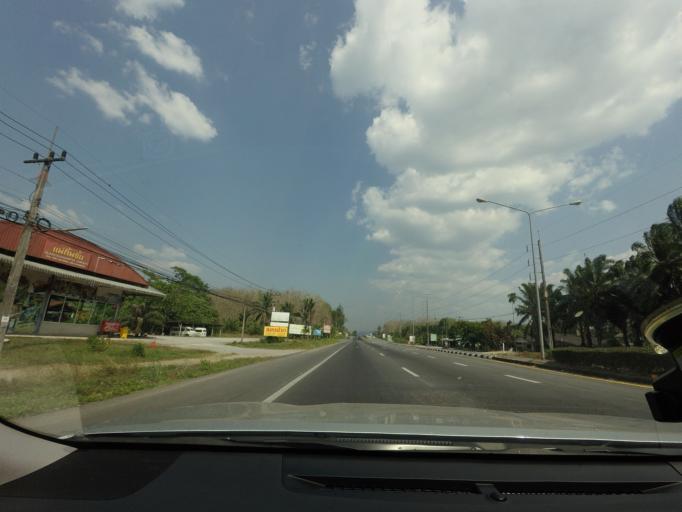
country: TH
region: Phangnga
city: Thap Put
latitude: 8.5091
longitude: 98.6535
